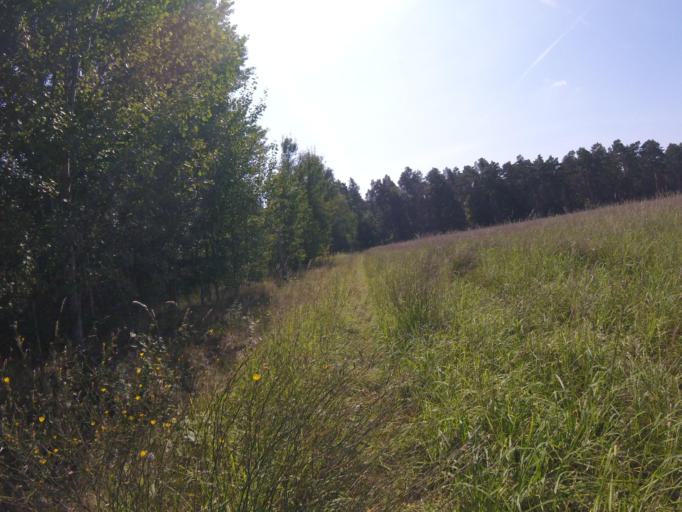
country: DE
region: Brandenburg
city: Bestensee
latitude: 52.2201
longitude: 13.7030
